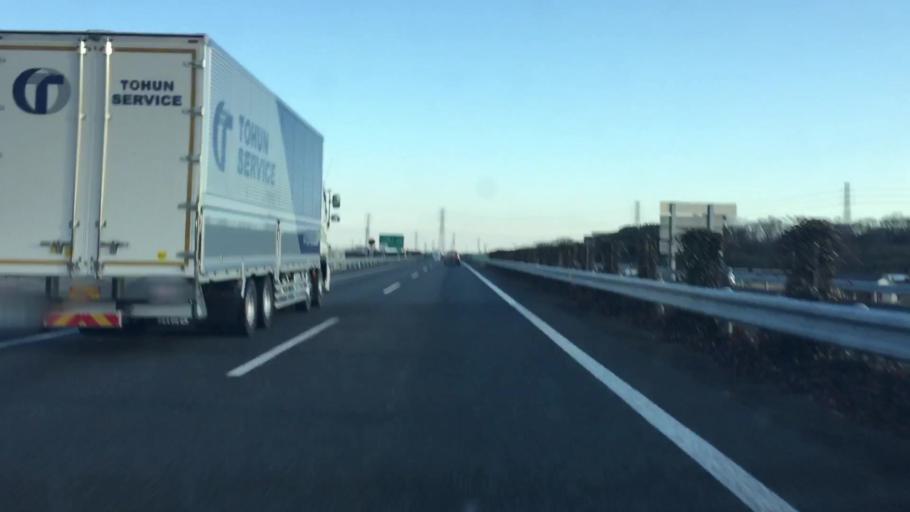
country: JP
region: Gunma
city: Ota
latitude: 36.3331
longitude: 139.3748
